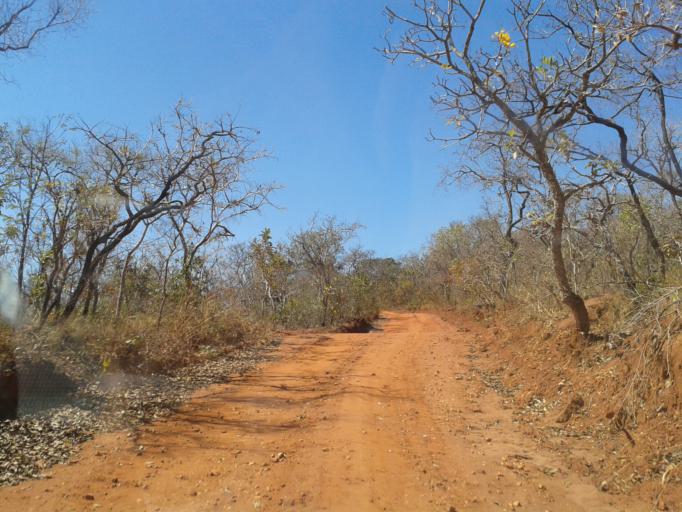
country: BR
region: Minas Gerais
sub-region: Monte Alegre De Minas
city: Monte Alegre de Minas
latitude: -18.8318
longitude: -49.1014
